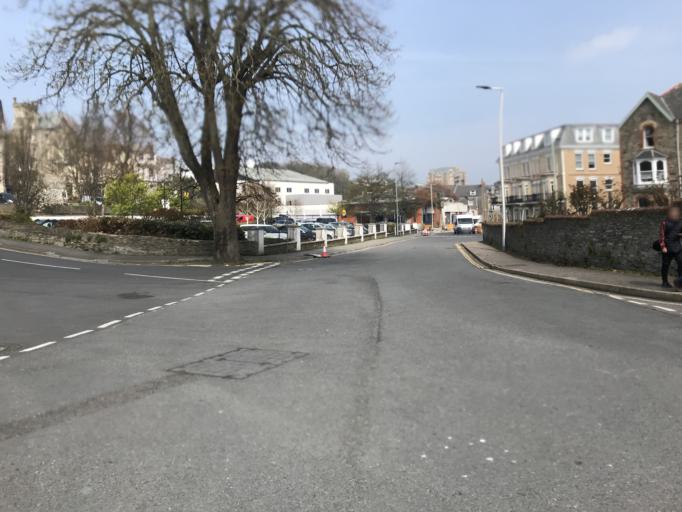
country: GB
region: England
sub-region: Devon
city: Ilfracombe
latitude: 51.2074
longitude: -4.1279
